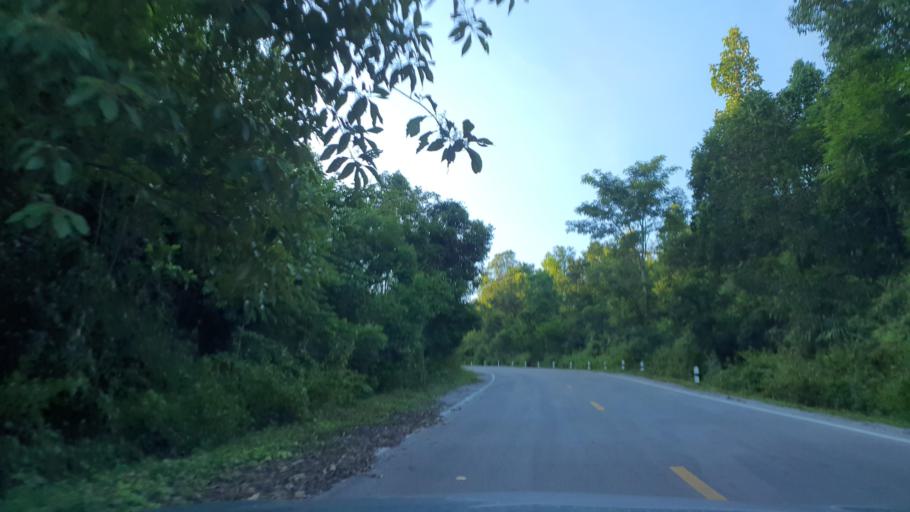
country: TH
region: Chiang Mai
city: Mae On
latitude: 18.8202
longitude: 99.3015
